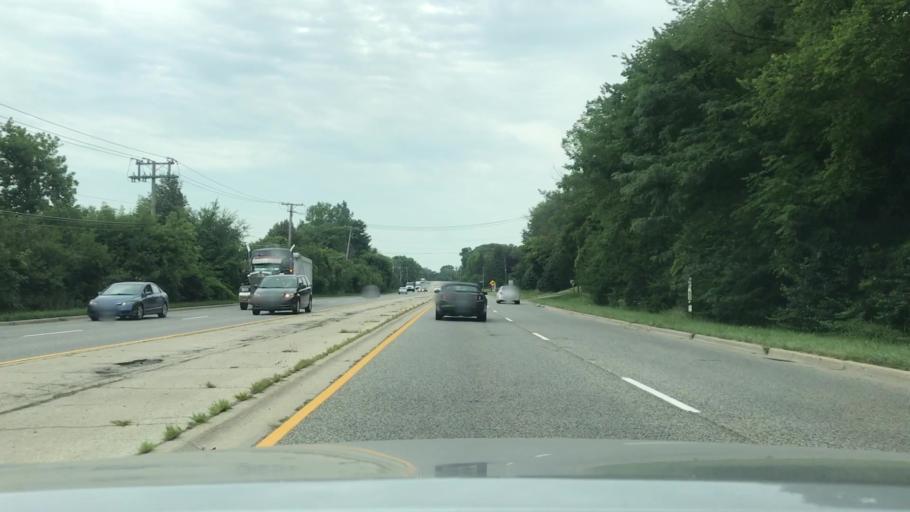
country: US
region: Illinois
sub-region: DuPage County
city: Woodridge
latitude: 41.7387
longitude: -88.0628
